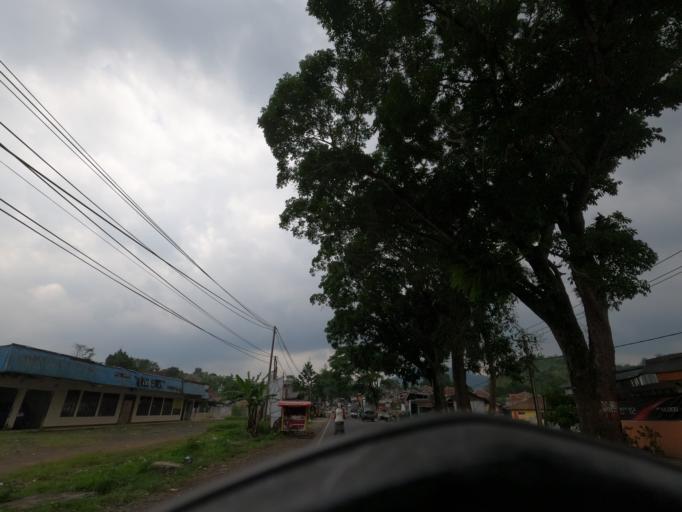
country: ID
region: West Java
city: Sukabumi
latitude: -6.7821
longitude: 107.0633
